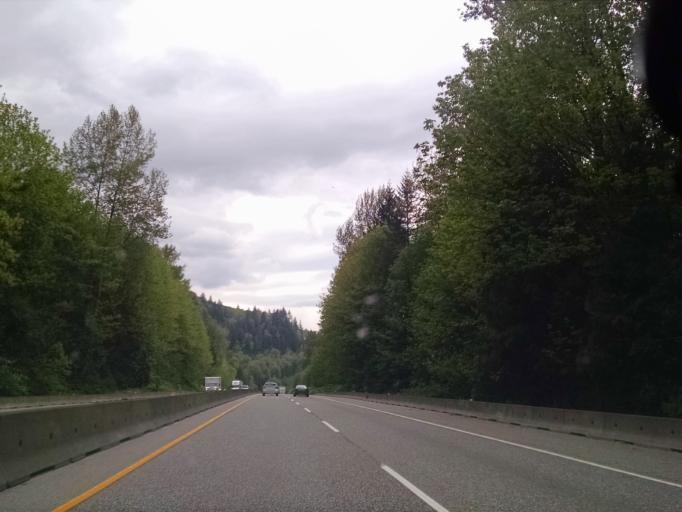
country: CA
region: British Columbia
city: Agassiz
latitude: 49.1656
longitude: -121.7895
